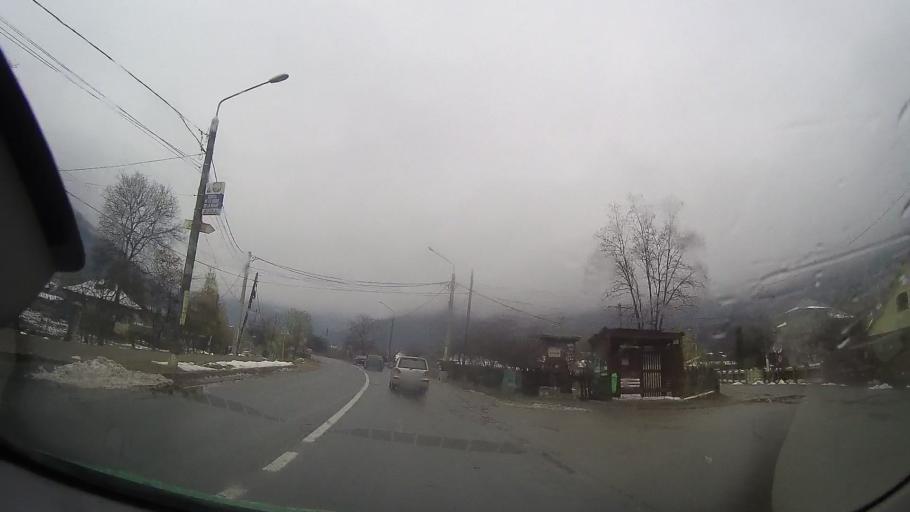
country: RO
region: Neamt
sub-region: Comuna Bicaz
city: Dodeni
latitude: 46.9057
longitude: 26.1083
